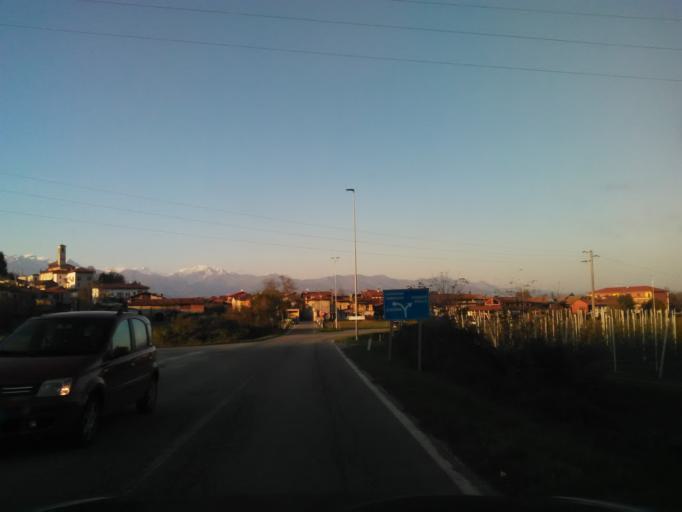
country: IT
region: Piedmont
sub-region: Provincia di Biella
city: Cerrione
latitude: 45.4657
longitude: 8.0696
